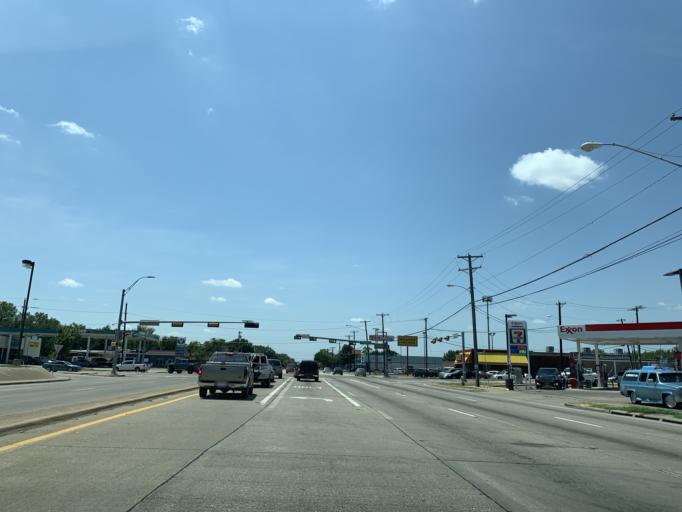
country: US
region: Texas
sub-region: Dallas County
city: Hutchins
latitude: 32.6950
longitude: -96.7714
